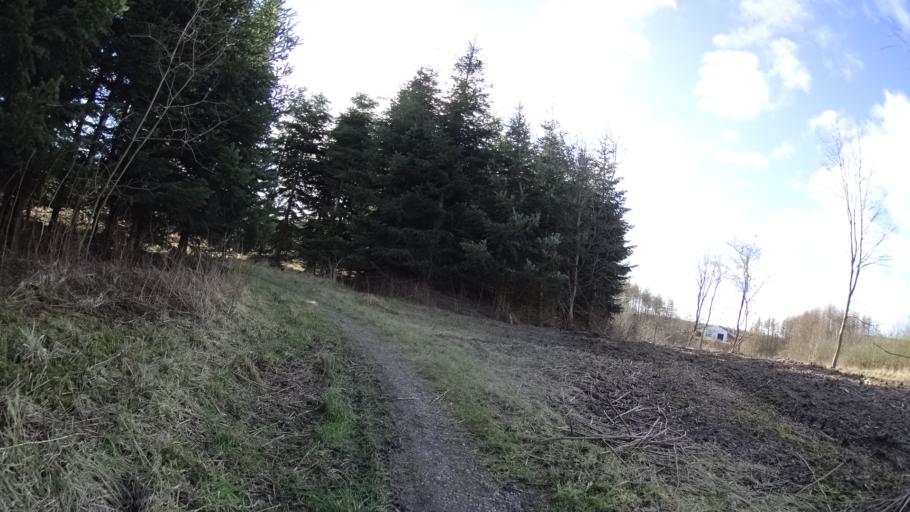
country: DK
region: Central Jutland
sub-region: Arhus Kommune
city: Tranbjerg
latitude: 56.1059
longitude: 10.1236
